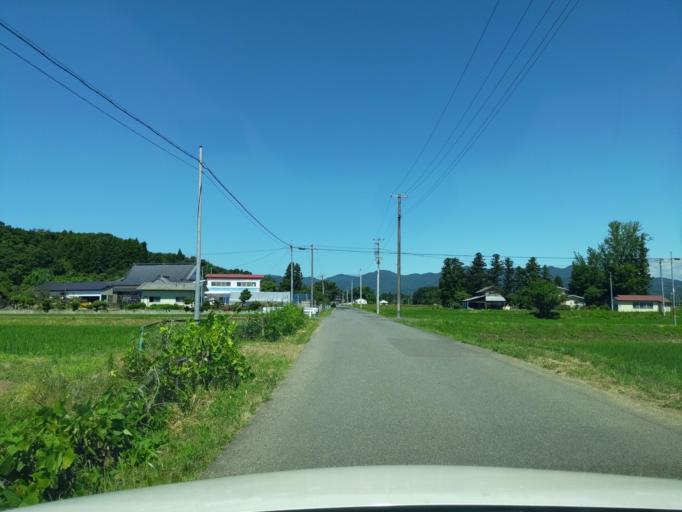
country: JP
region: Fukushima
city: Koriyama
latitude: 37.3868
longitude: 140.2903
